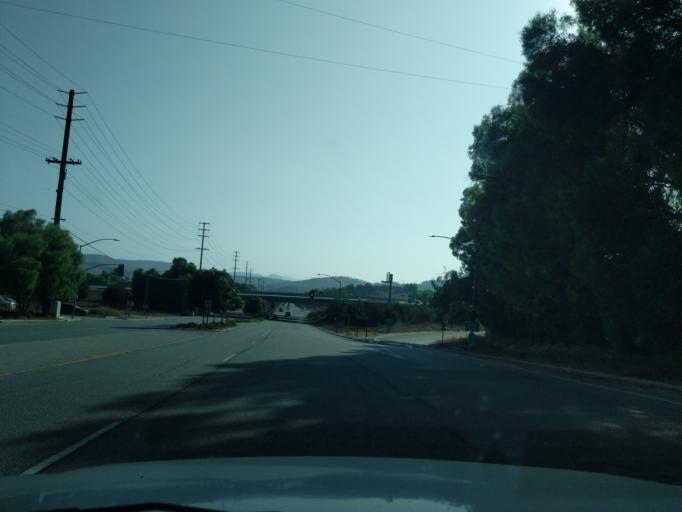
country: US
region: California
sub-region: Ventura County
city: Moorpark
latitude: 34.2680
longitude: -118.8495
